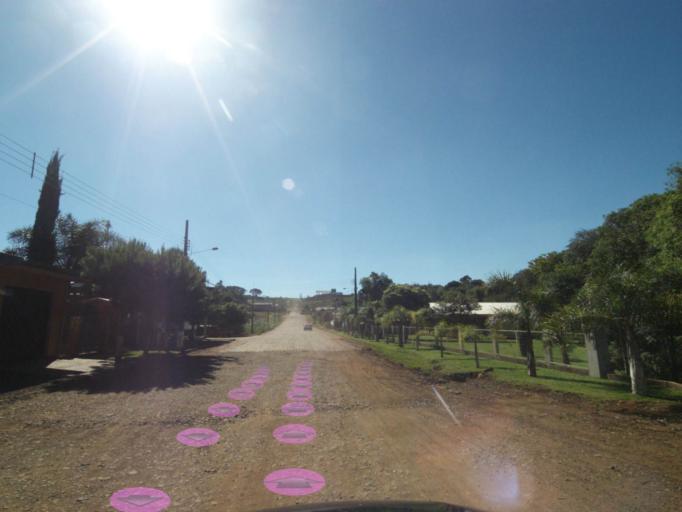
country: BR
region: Parana
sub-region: Coronel Vivida
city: Coronel Vivida
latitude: -26.1417
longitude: -52.3855
